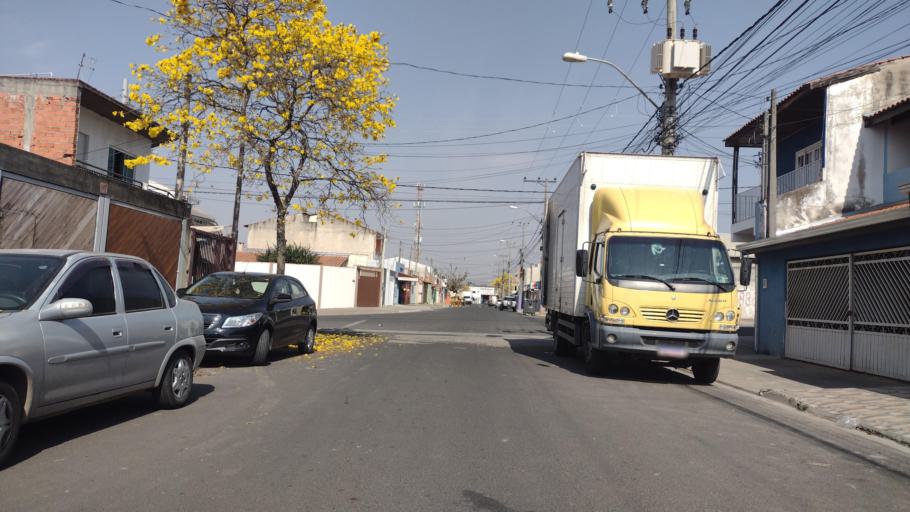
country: BR
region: Sao Paulo
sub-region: Sorocaba
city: Sorocaba
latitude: -23.4295
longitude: -47.4643
